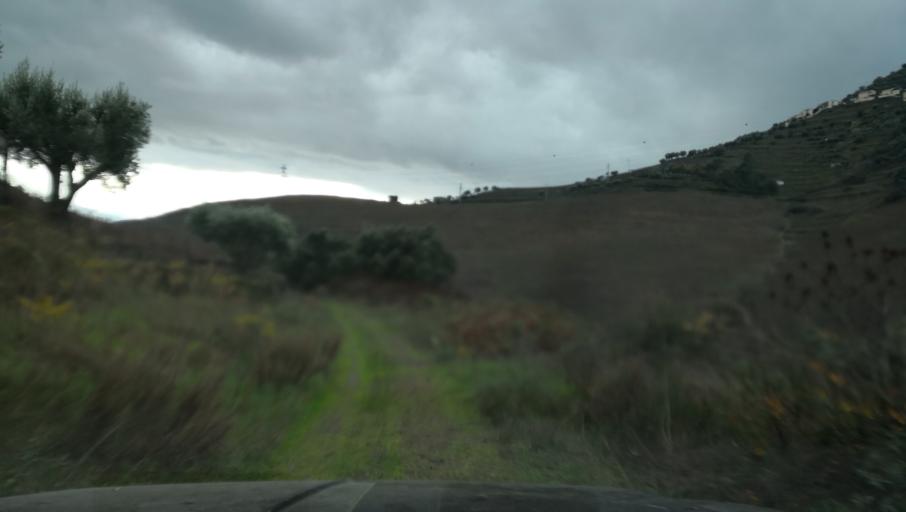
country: PT
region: Vila Real
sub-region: Peso da Regua
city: Peso da Regua
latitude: 41.1847
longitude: -7.7595
